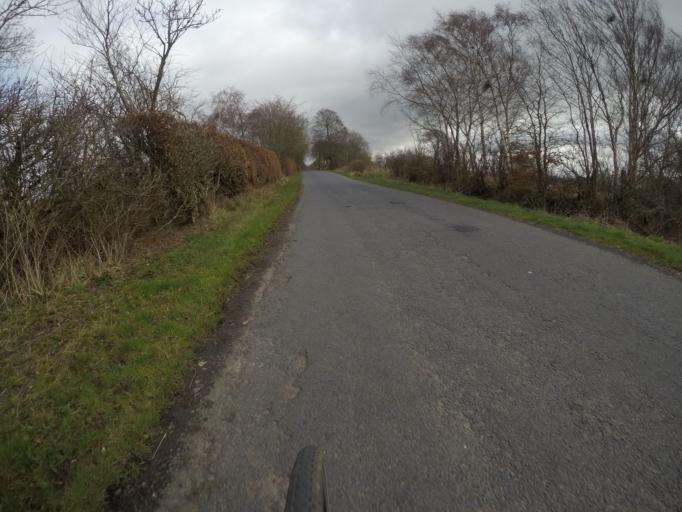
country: GB
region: Scotland
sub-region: North Ayrshire
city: Springside
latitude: 55.6691
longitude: -4.5804
